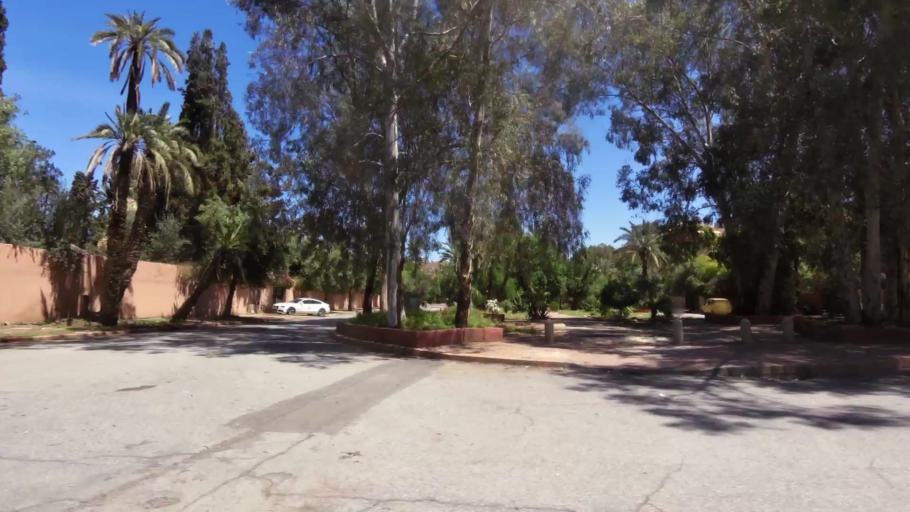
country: MA
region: Marrakech-Tensift-Al Haouz
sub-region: Marrakech
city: Marrakesh
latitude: 31.6226
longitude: -8.0093
